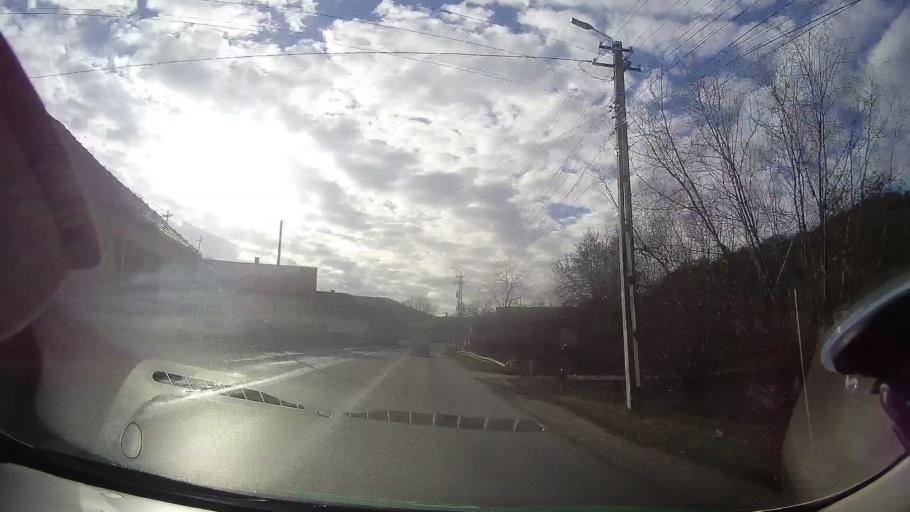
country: RO
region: Cluj
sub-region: Comuna Savadisla
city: Savadisla
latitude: 46.6780
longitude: 23.4567
